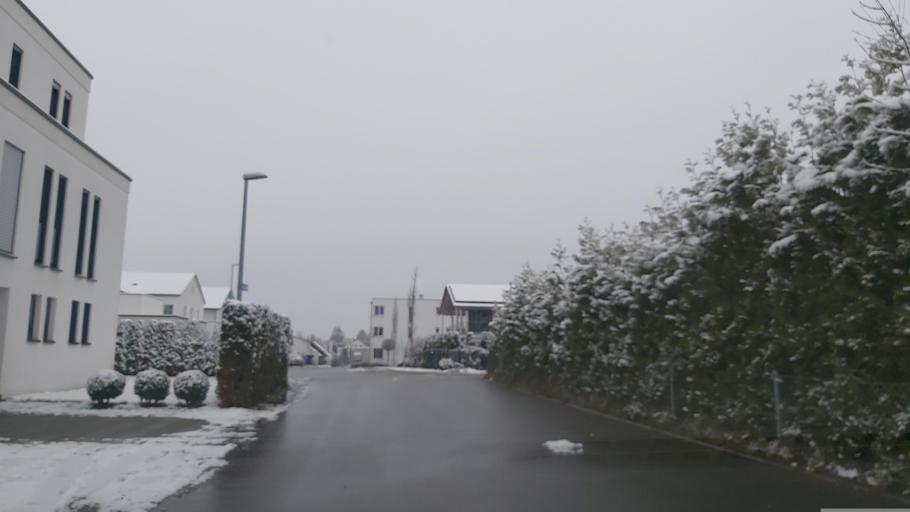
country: DE
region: Baden-Wuerttemberg
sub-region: Tuebingen Region
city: Laupheim
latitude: 48.2377
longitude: 9.8971
